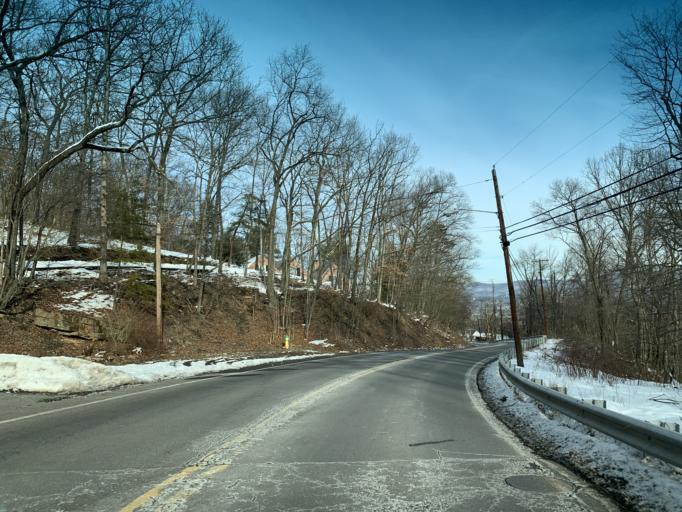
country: US
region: Maryland
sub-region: Allegany County
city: La Vale
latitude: 39.6451
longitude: -78.7952
